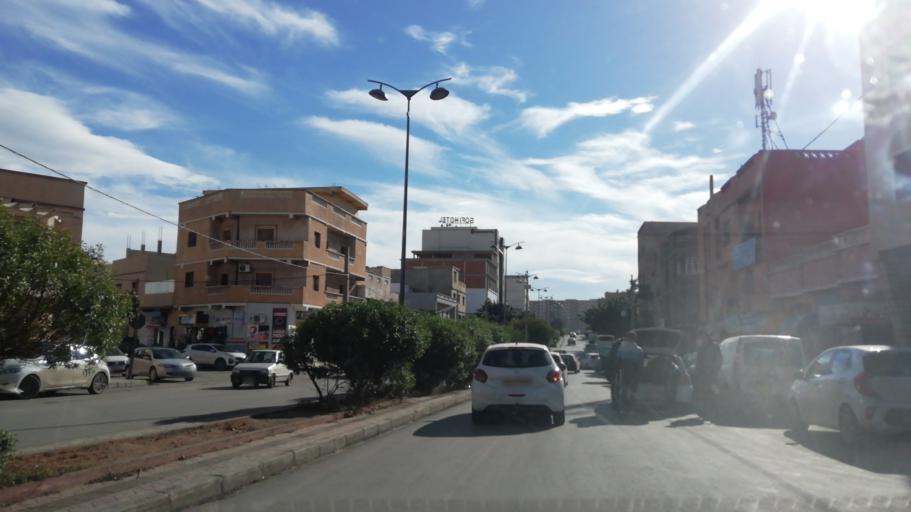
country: DZ
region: Oran
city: Oran
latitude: 35.6944
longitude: -0.6198
